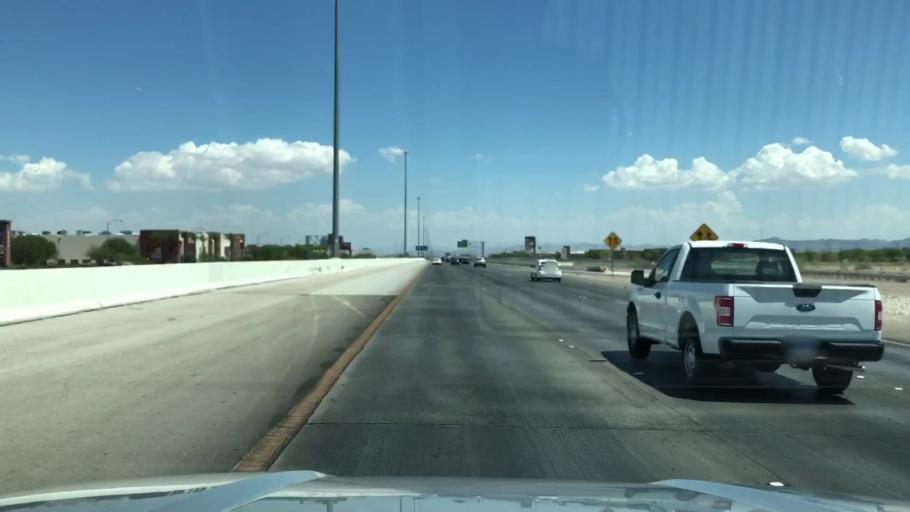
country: US
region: Nevada
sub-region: Clark County
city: Spring Valley
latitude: 36.0662
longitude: -115.2574
